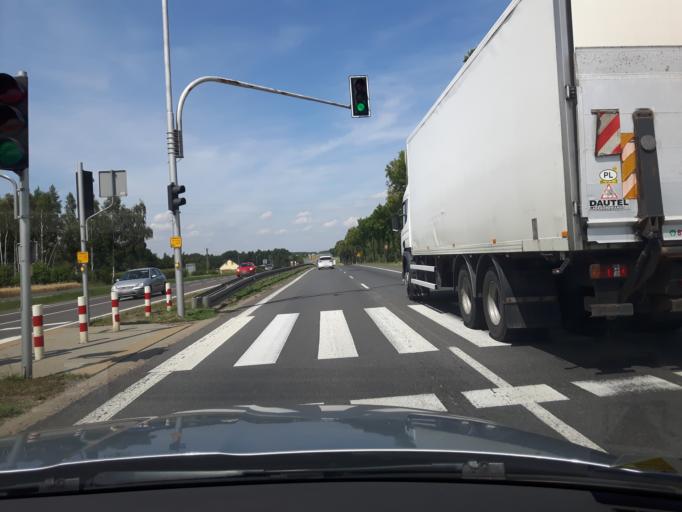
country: PL
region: Masovian Voivodeship
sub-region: Powiat plonski
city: Zaluski
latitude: 52.5601
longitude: 20.4929
